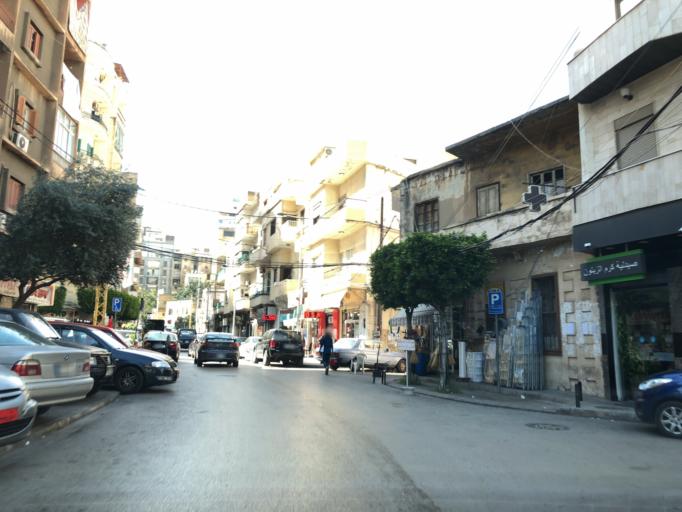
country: LB
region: Beyrouth
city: Beirut
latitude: 33.8884
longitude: 35.5281
